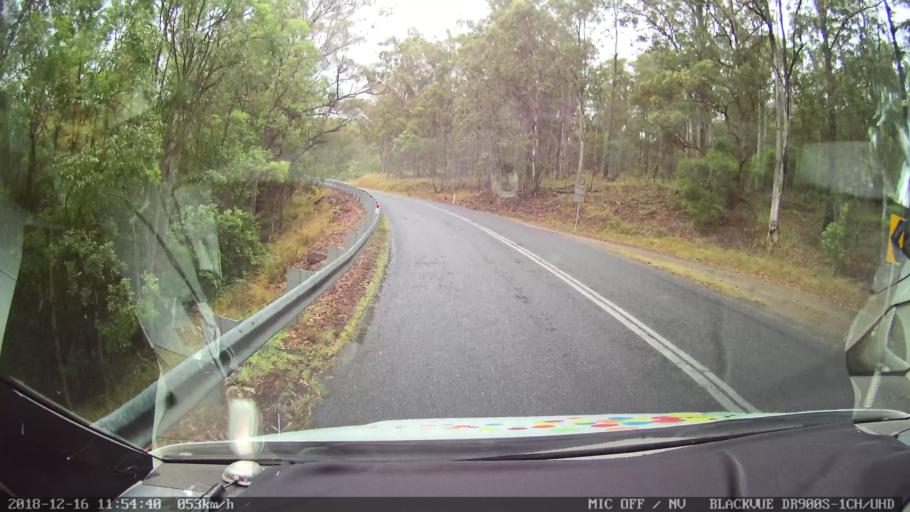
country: AU
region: New South Wales
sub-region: Tenterfield Municipality
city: Carrolls Creek
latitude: -28.9102
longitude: 152.2862
